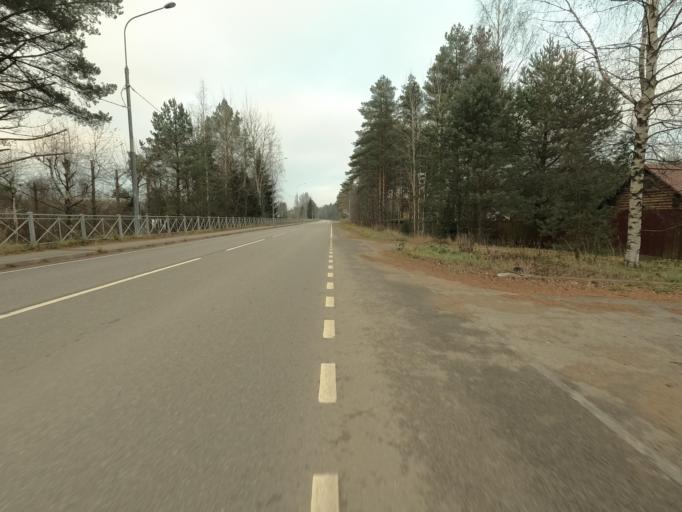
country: RU
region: Leningrad
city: Pavlovo
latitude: 59.8041
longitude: 30.9578
